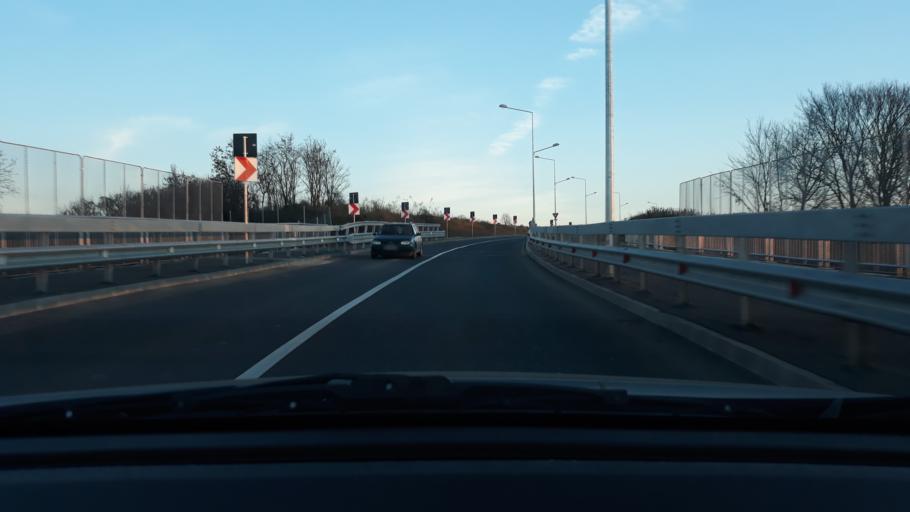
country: RO
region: Bihor
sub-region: Comuna Biharea
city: Biharea
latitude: 47.1112
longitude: 21.9041
